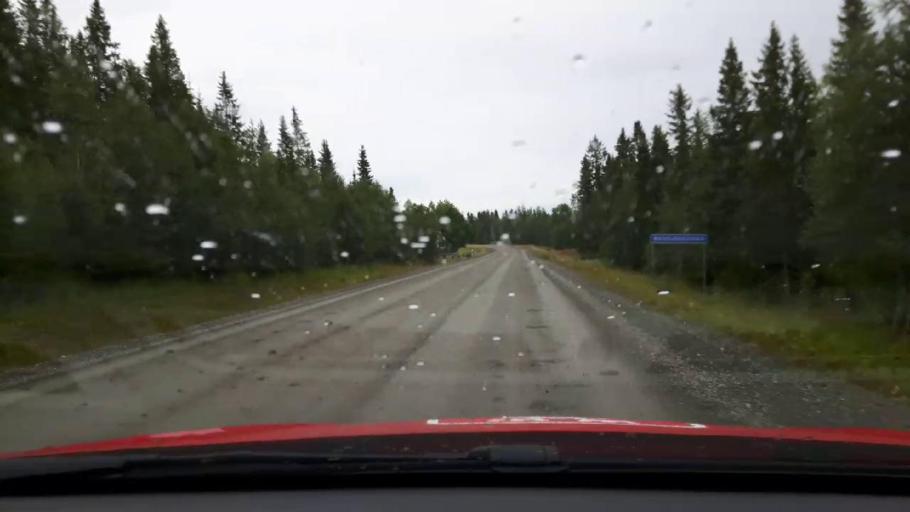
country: SE
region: Jaemtland
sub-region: Are Kommun
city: Are
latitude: 63.4652
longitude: 12.6192
